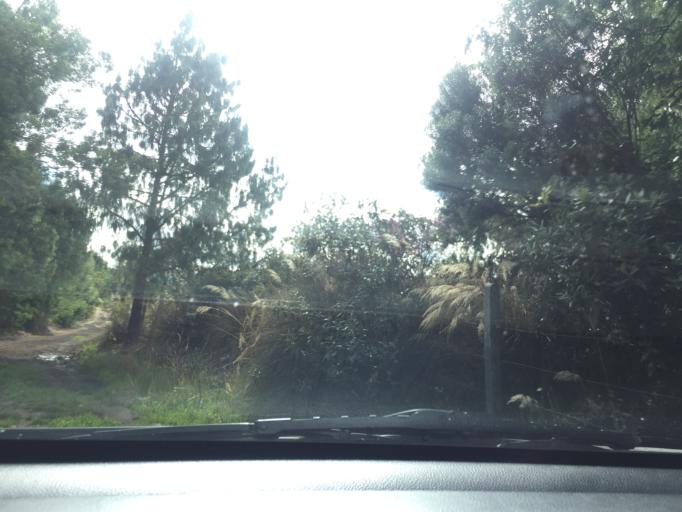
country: CO
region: Cundinamarca
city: Tocancipa
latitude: 4.9486
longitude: -73.8906
